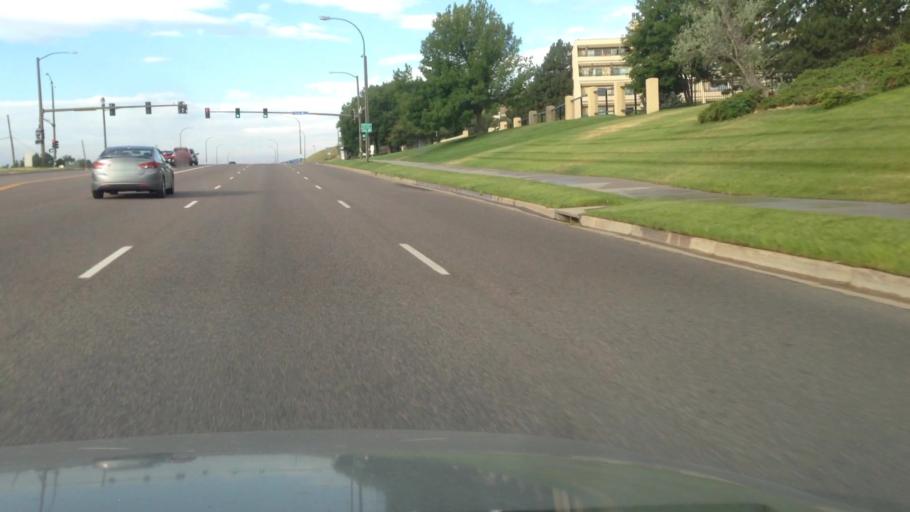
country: US
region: Colorado
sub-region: Jefferson County
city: West Pleasant View
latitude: 39.6942
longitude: -105.1478
